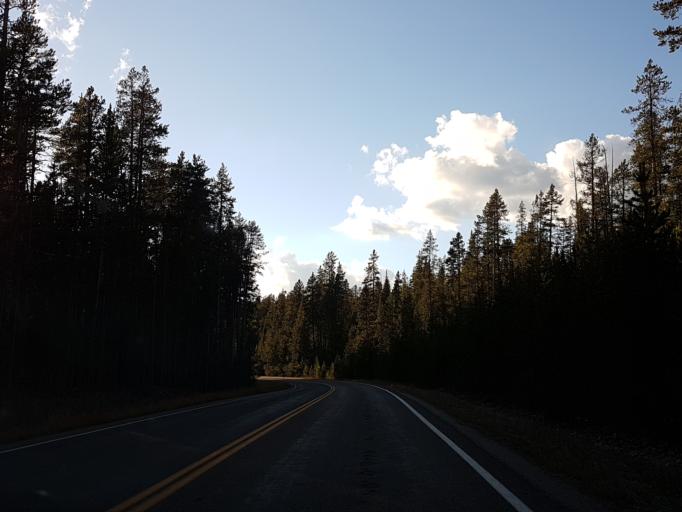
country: US
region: Montana
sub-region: Gallatin County
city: West Yellowstone
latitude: 44.4315
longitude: -110.7560
